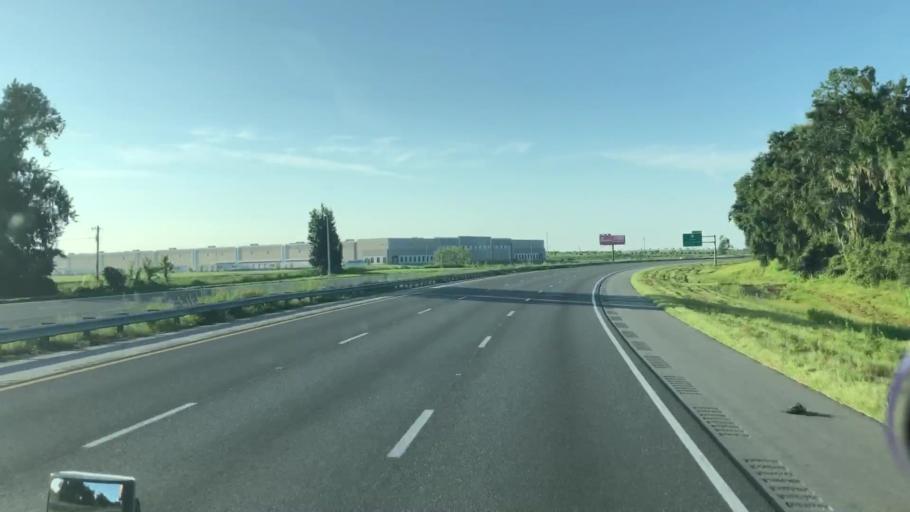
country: US
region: Florida
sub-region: Marion County
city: Ocala
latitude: 29.2275
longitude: -82.1857
